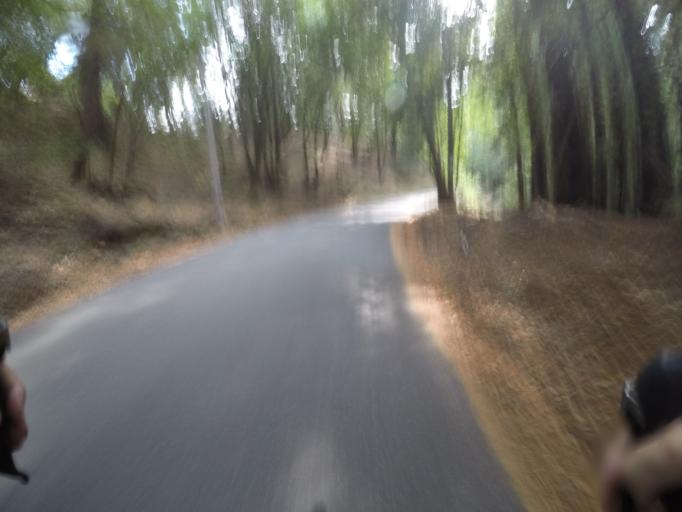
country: US
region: California
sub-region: Santa Cruz County
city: Scotts Valley
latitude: 37.0835
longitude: -122.0098
